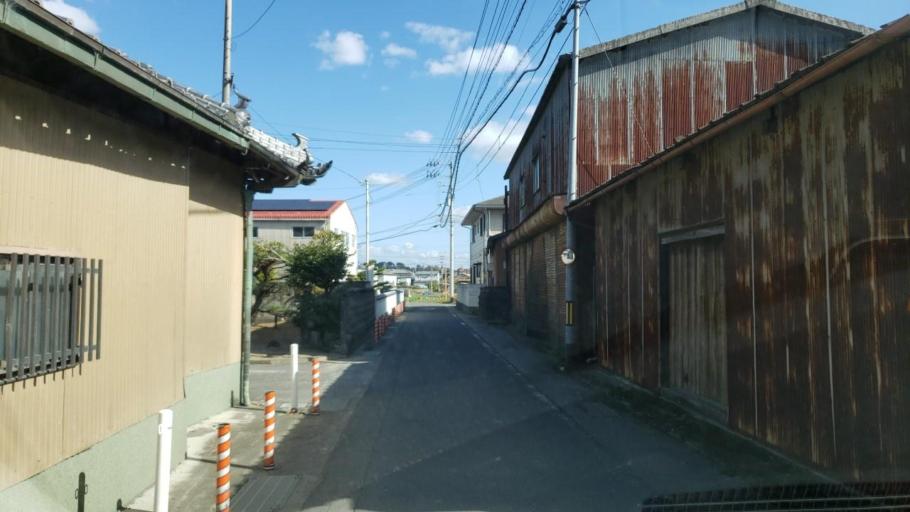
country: JP
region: Tokushima
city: Wakimachi
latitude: 34.0789
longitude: 134.1984
